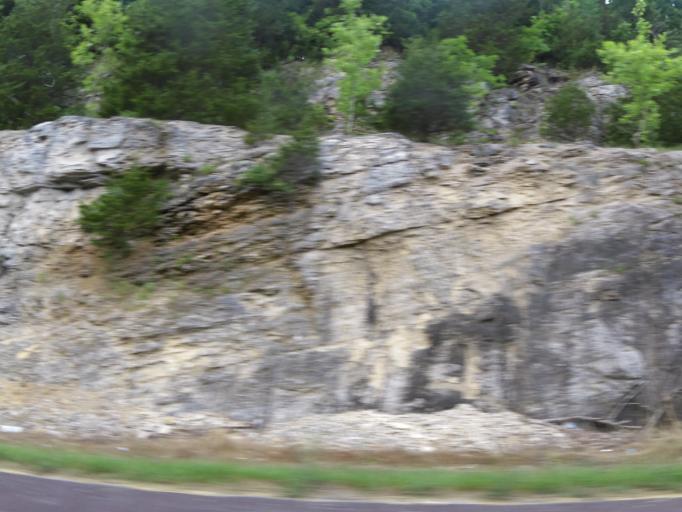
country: US
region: Missouri
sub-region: Saint Louis County
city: Eureka
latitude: 38.4879
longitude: -90.6328
